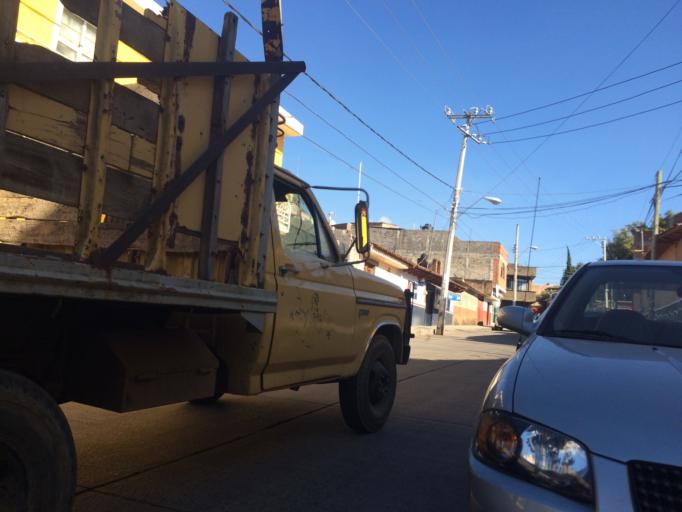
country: MX
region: Michoacan
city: Patzcuaro
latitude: 19.5126
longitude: -101.6021
